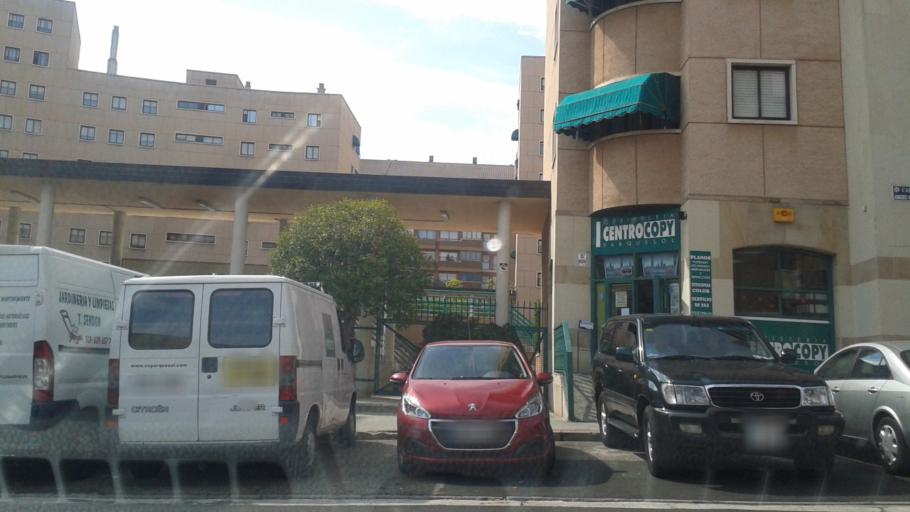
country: ES
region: Castille and Leon
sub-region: Provincia de Valladolid
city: Zaratan
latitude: 41.6348
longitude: -4.7570
